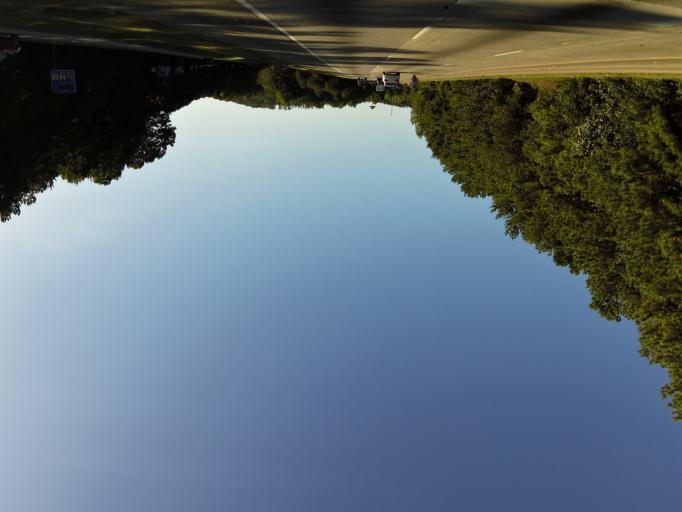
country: US
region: Georgia
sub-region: Cobb County
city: Kennesaw
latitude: 34.0136
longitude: -84.5696
